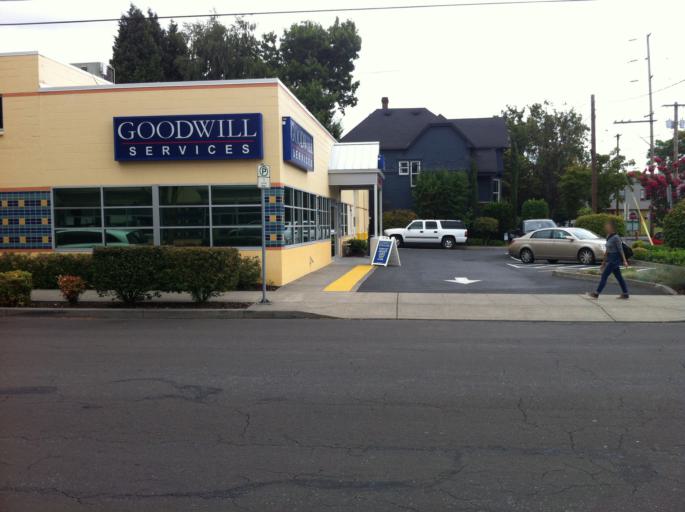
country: US
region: Oregon
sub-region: Multnomah County
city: Portland
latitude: 45.5088
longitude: -122.6597
